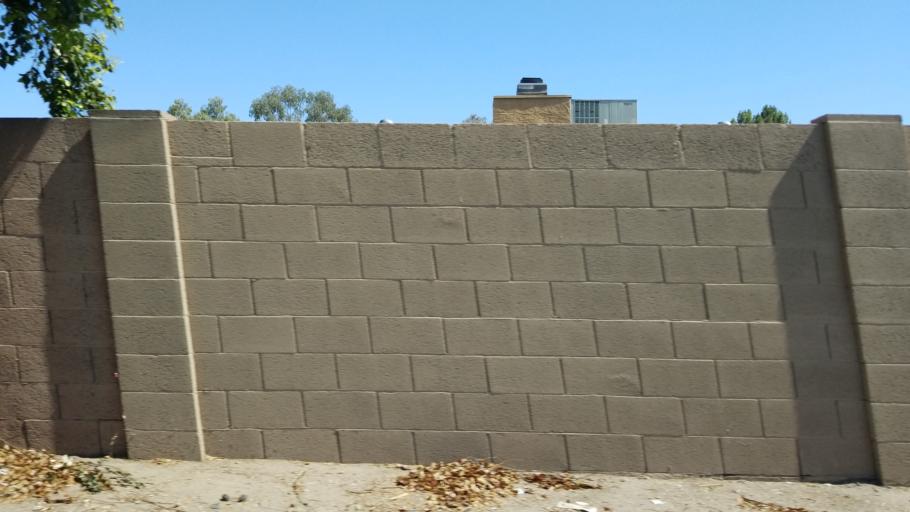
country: US
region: Arizona
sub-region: Maricopa County
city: Tolleson
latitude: 33.4946
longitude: -112.2306
